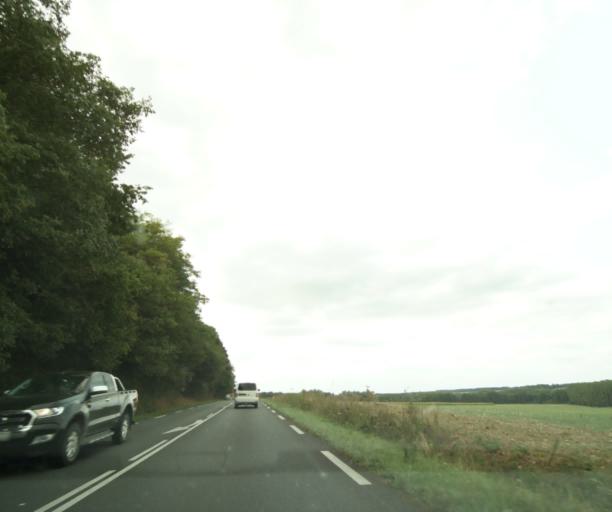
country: FR
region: Centre
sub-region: Departement d'Indre-et-Loire
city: Chambourg-sur-Indre
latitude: 47.1673
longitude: 0.9823
